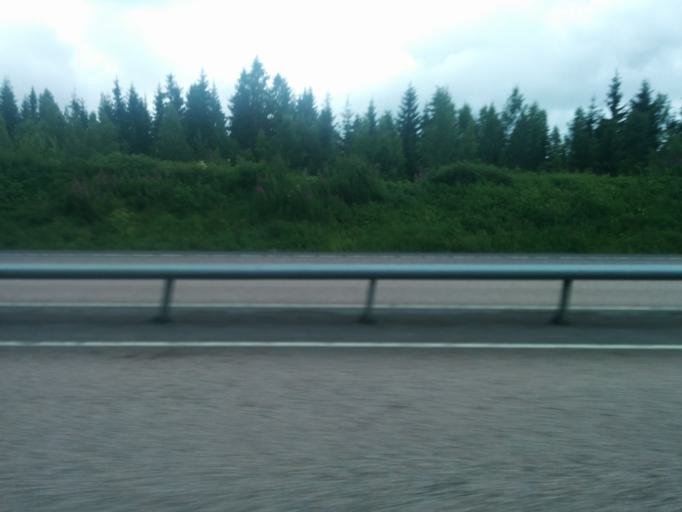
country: FI
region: Pirkanmaa
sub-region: Tampere
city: Orivesi
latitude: 61.7061
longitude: 24.5471
